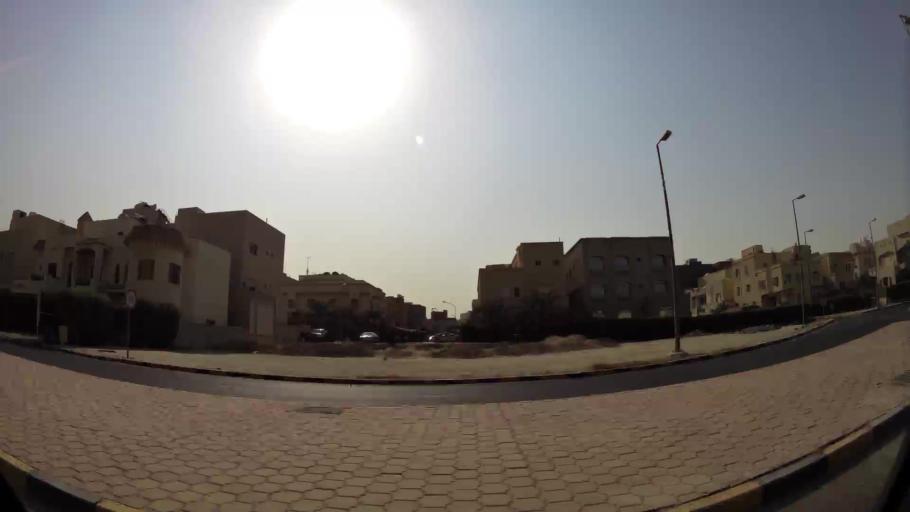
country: KW
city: Bayan
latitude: 29.2798
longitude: 48.0423
